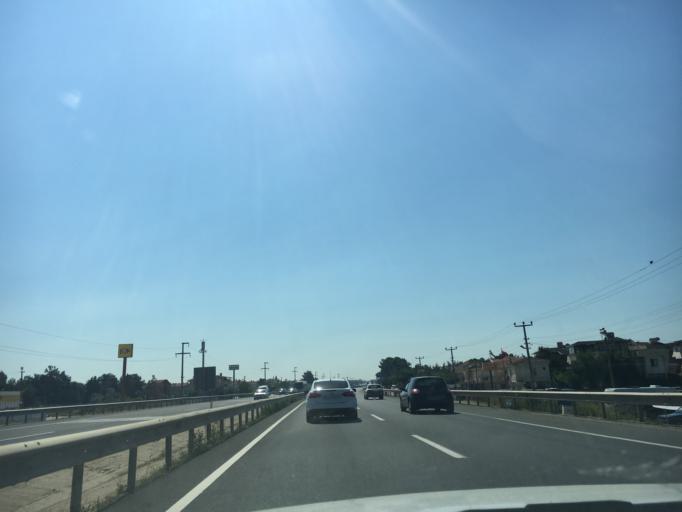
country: TR
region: Tekirdag
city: Marmara Ereglisi
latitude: 40.9930
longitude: 27.8439
